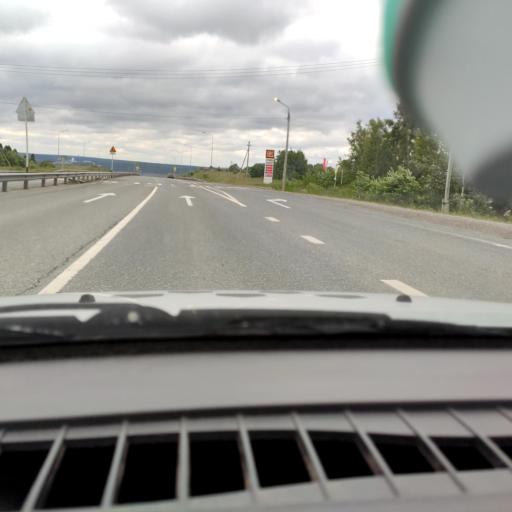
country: RU
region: Perm
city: Polazna
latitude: 58.2003
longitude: 56.4022
